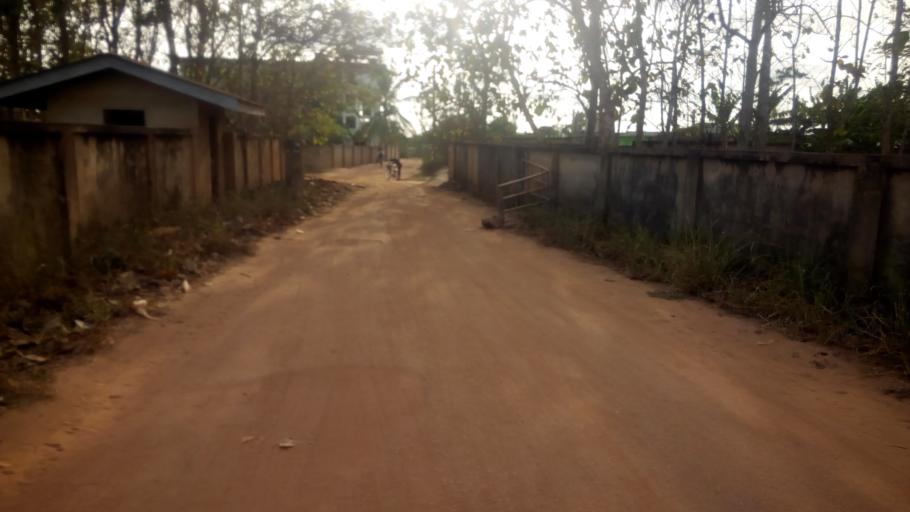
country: GH
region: Central
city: Cape Coast
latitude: 5.1265
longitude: -1.2949
